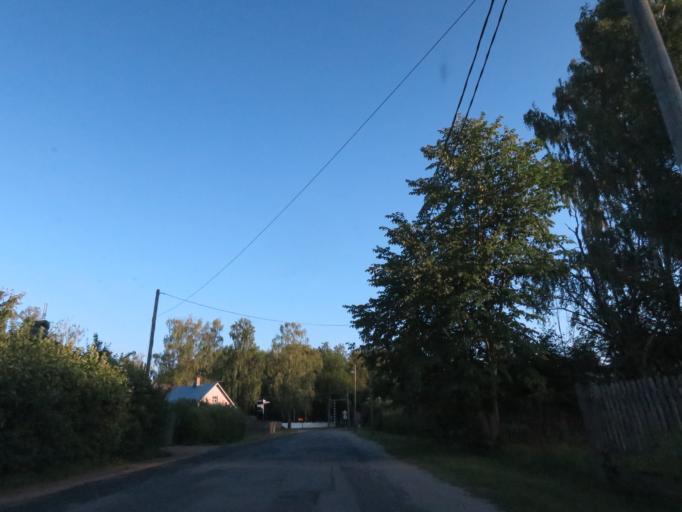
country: LV
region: Sigulda
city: Sigulda
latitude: 57.1672
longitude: 24.8616
